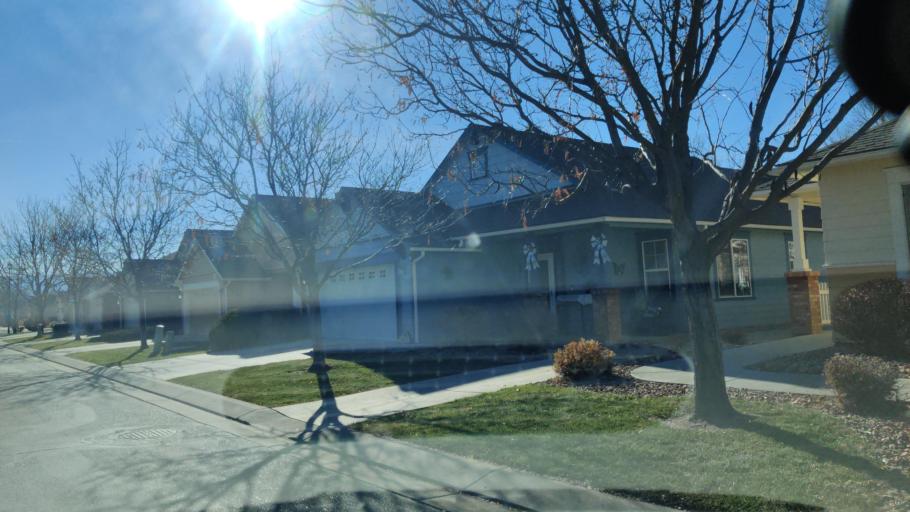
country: US
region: Colorado
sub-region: Mesa County
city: Redlands
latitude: 39.1114
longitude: -108.5936
